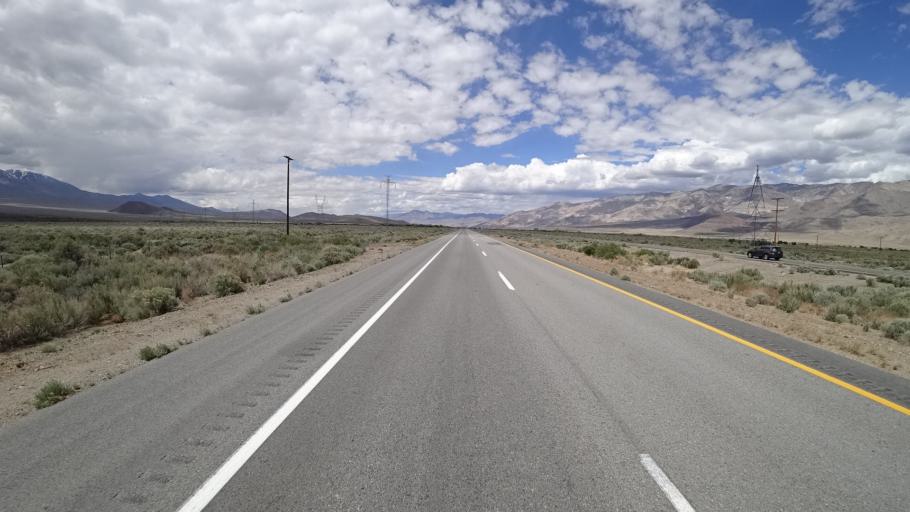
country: US
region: California
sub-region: Inyo County
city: Big Pine
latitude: 36.9745
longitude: -118.2373
